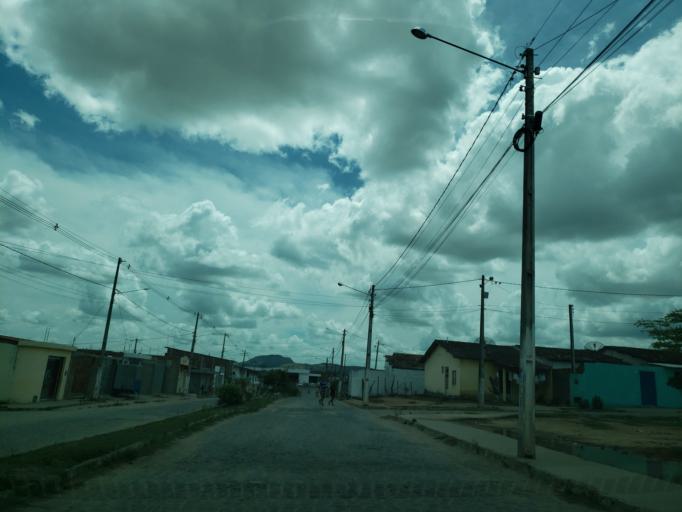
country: BR
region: Alagoas
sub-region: Uniao Dos Palmares
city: Uniao dos Palmares
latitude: -9.1511
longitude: -36.0111
